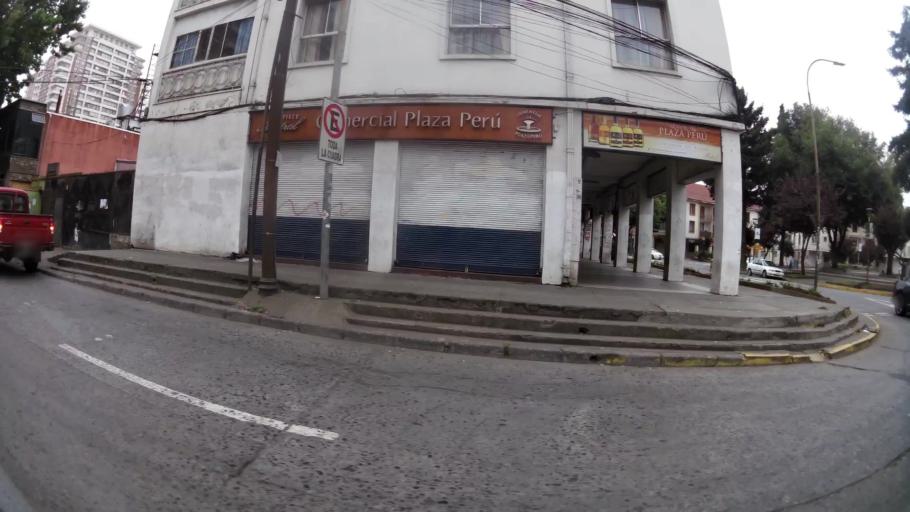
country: CL
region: Biobio
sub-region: Provincia de Concepcion
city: Concepcion
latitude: -36.8272
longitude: -73.0402
